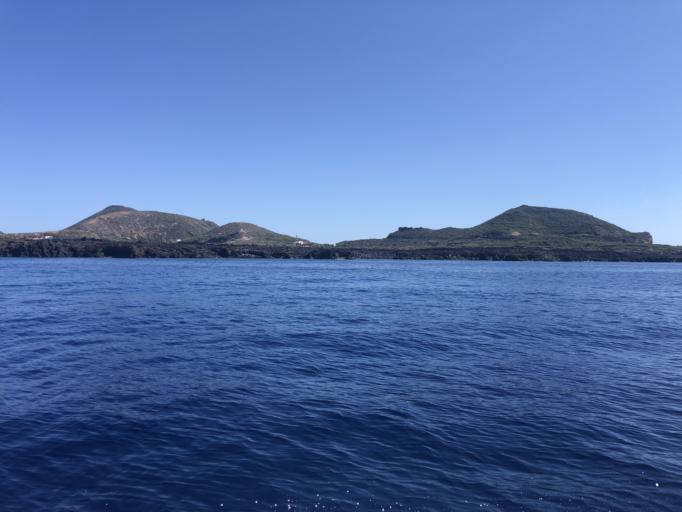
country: IT
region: Sicily
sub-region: Agrigento
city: Lampedusa
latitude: 35.8758
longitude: 12.8552
